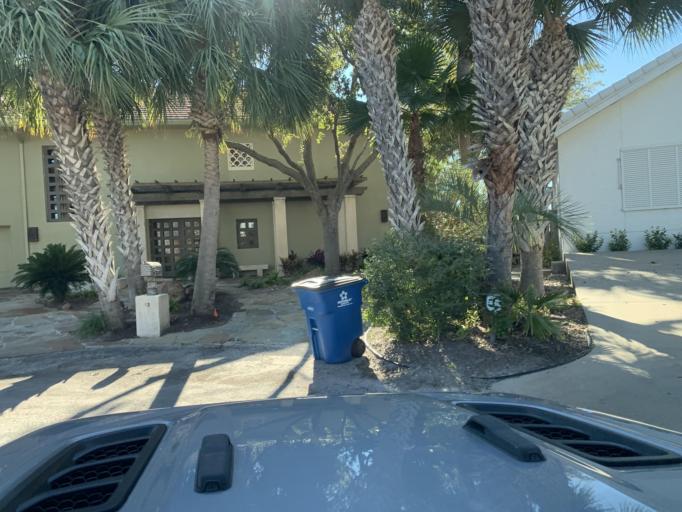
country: US
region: Texas
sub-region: Aransas County
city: Fulton
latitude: 28.0379
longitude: -97.0316
